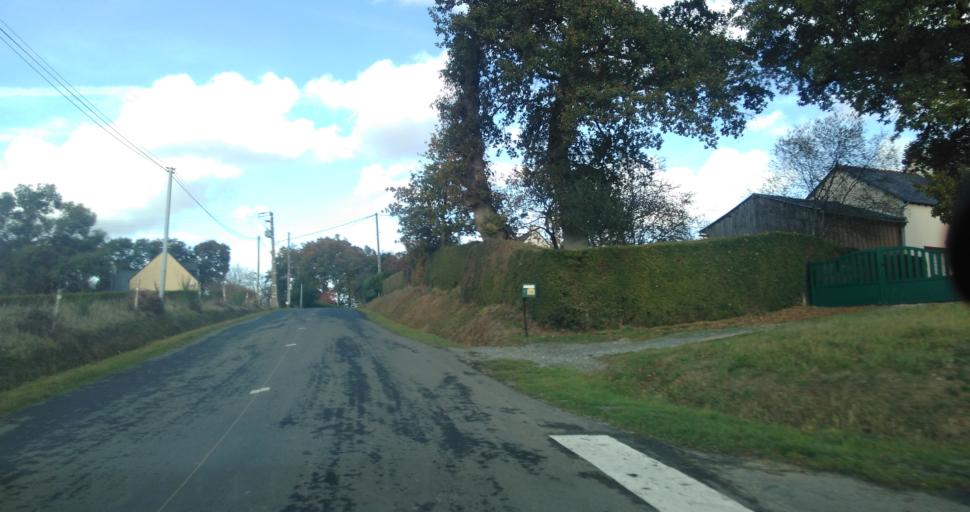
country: FR
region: Brittany
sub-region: Departement d'Ille-et-Vilaine
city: Boisgervilly
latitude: 48.1368
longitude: -2.0820
